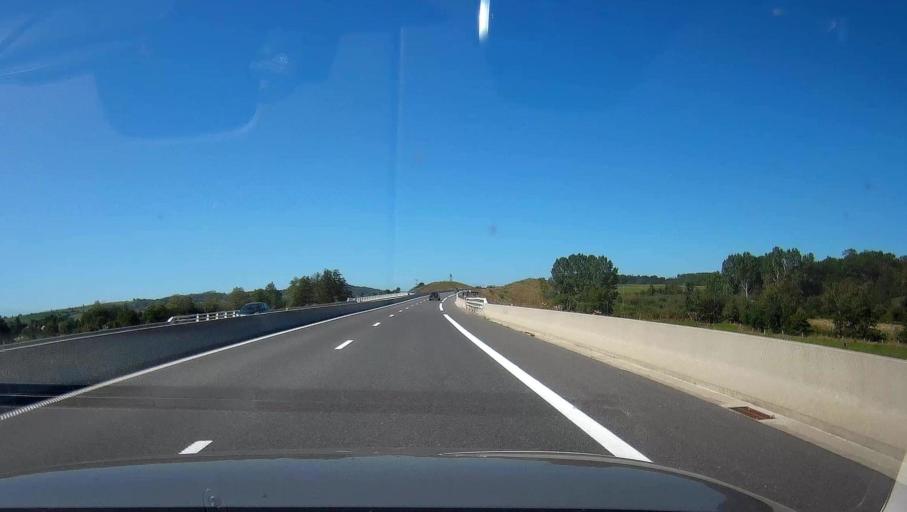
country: FR
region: Champagne-Ardenne
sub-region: Departement des Ardennes
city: Rimogne
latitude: 49.7951
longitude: 4.5387
